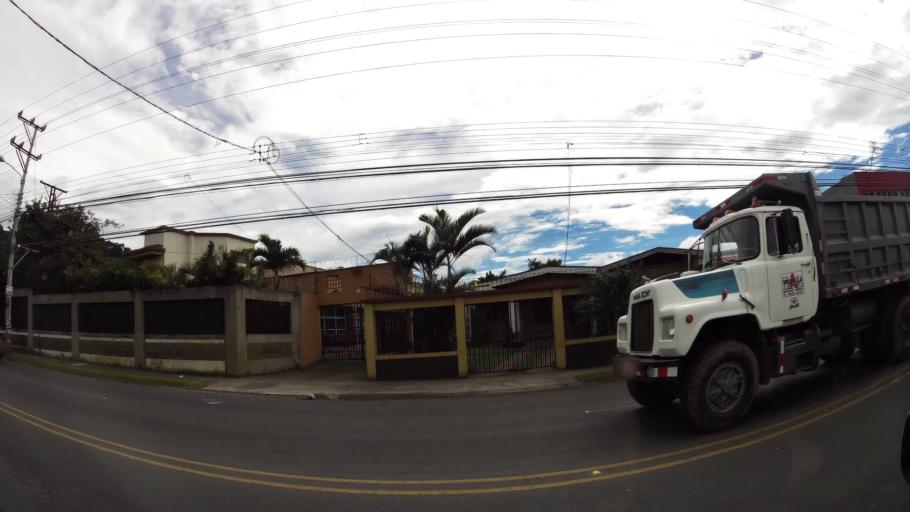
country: CR
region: San Jose
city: Curridabat
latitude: 9.9005
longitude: -84.0458
